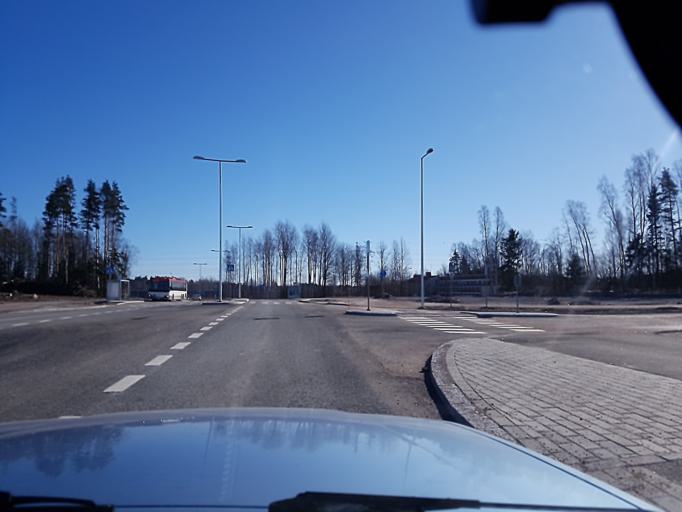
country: FI
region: Uusimaa
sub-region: Helsinki
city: Kilo
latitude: 60.2952
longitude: 24.8492
